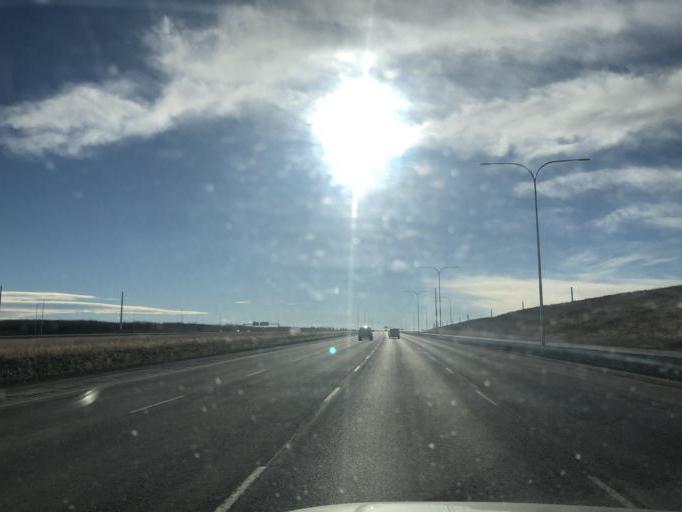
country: CA
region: Alberta
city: Calgary
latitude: 50.9742
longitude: -114.1562
